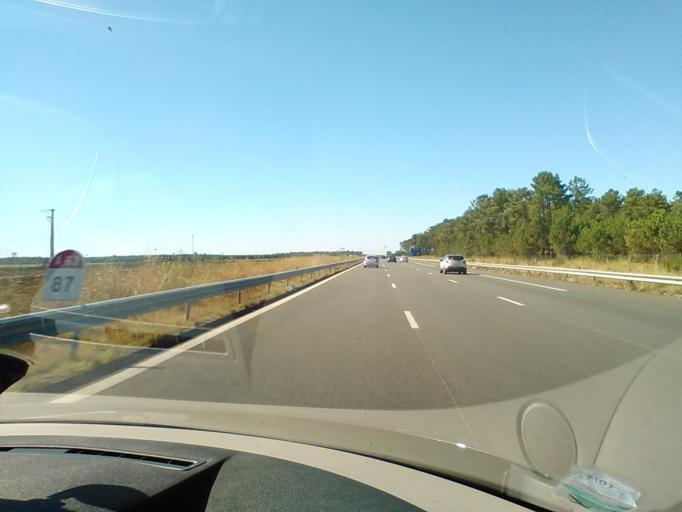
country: FR
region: Aquitaine
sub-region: Departement des Landes
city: Onesse-Laharie
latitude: 44.1123
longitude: -0.9892
